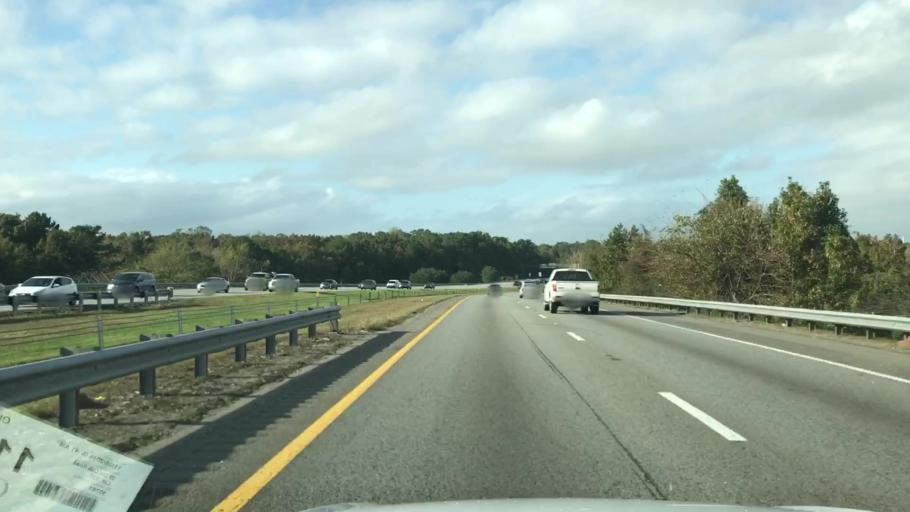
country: US
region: South Carolina
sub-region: Charleston County
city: North Charleston
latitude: 32.8635
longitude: -80.0261
